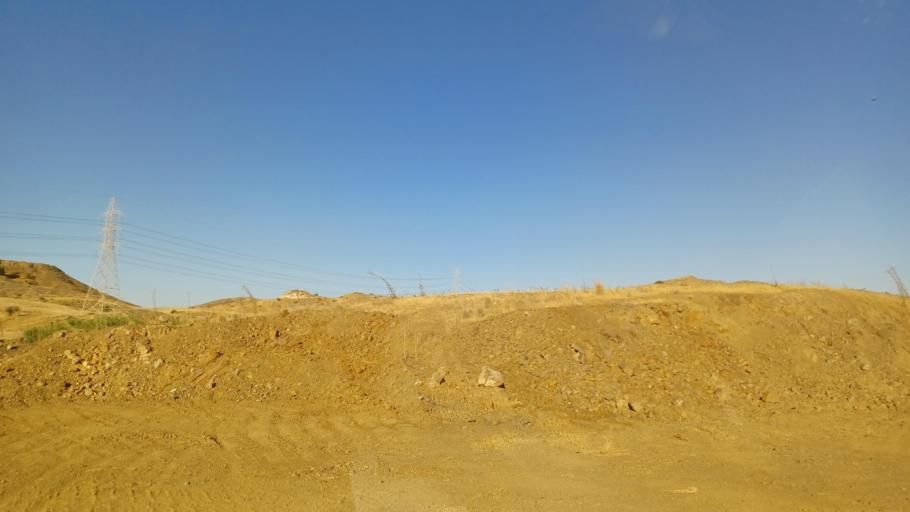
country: CY
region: Larnaka
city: Voroklini
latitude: 35.0044
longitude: 33.6397
